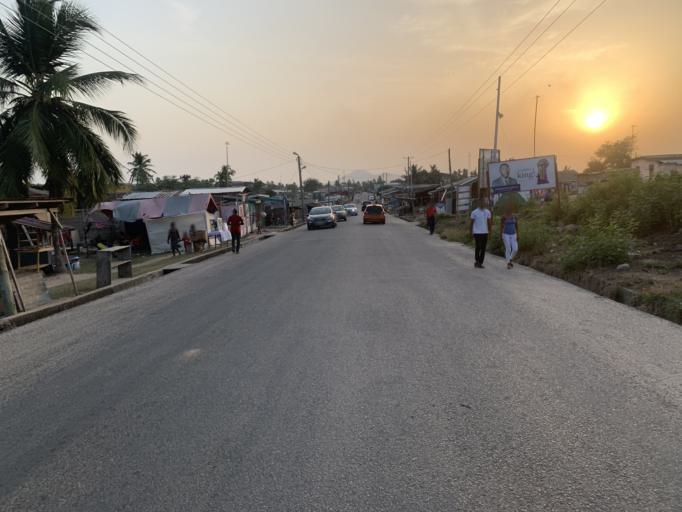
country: GH
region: Central
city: Winneba
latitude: 5.3519
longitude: -0.6197
